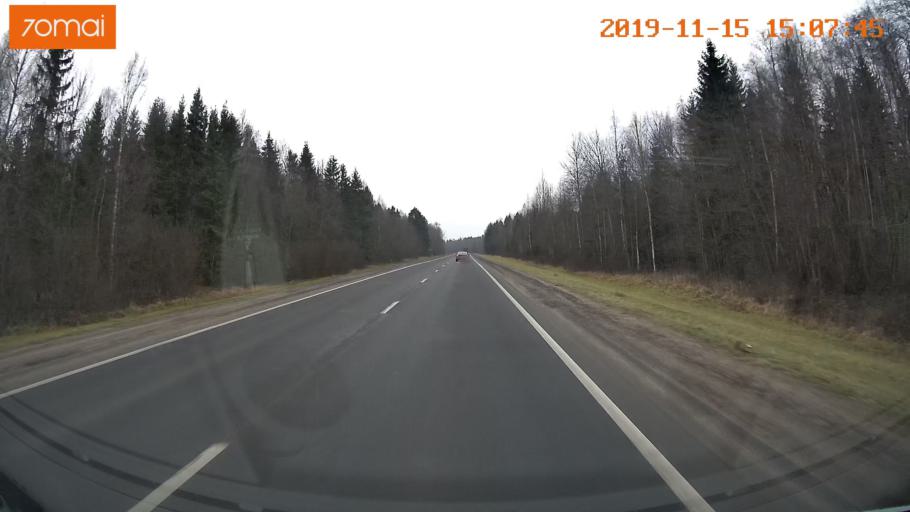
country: RU
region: Jaroslavl
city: Prechistoye
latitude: 58.3798
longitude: 40.2889
